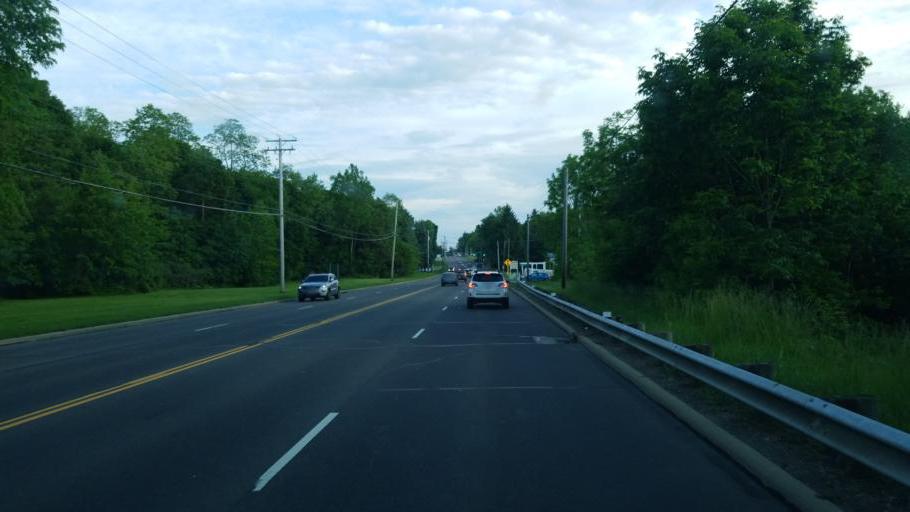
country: US
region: Ohio
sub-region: Stark County
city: Greentown
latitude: 40.9173
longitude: -81.4050
